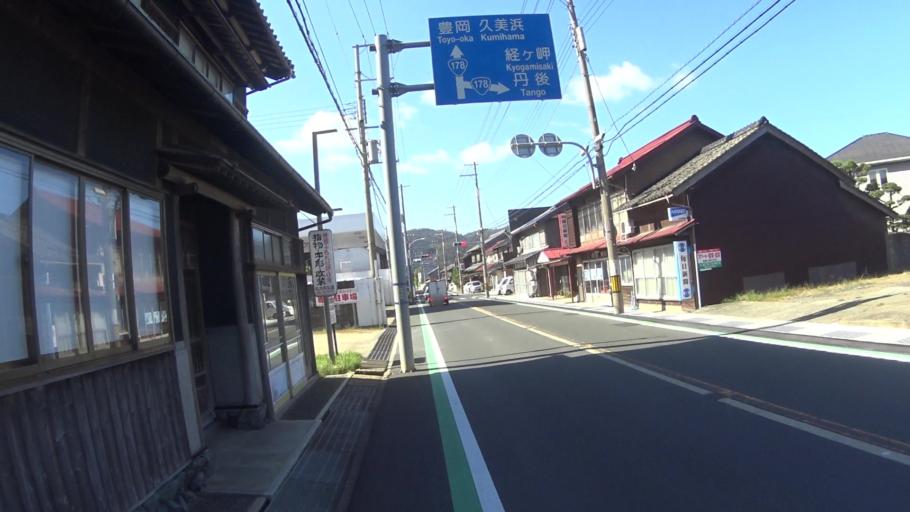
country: JP
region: Kyoto
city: Miyazu
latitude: 35.6802
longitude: 135.0310
